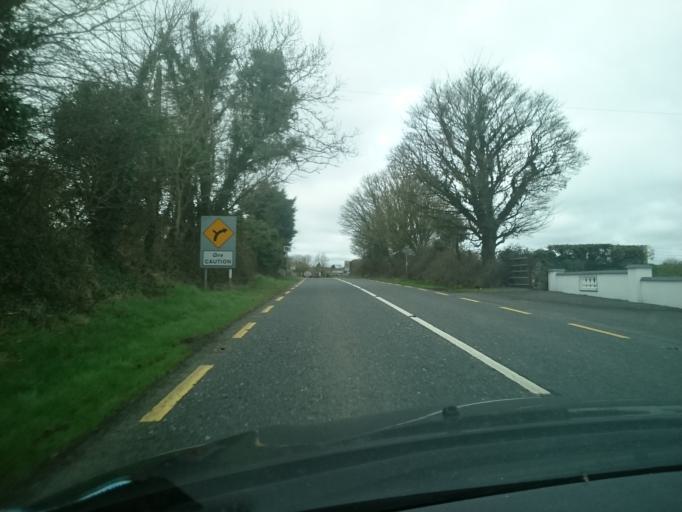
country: IE
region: Connaught
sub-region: Maigh Eo
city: Kiltamagh
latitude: 53.8008
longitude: -9.1210
